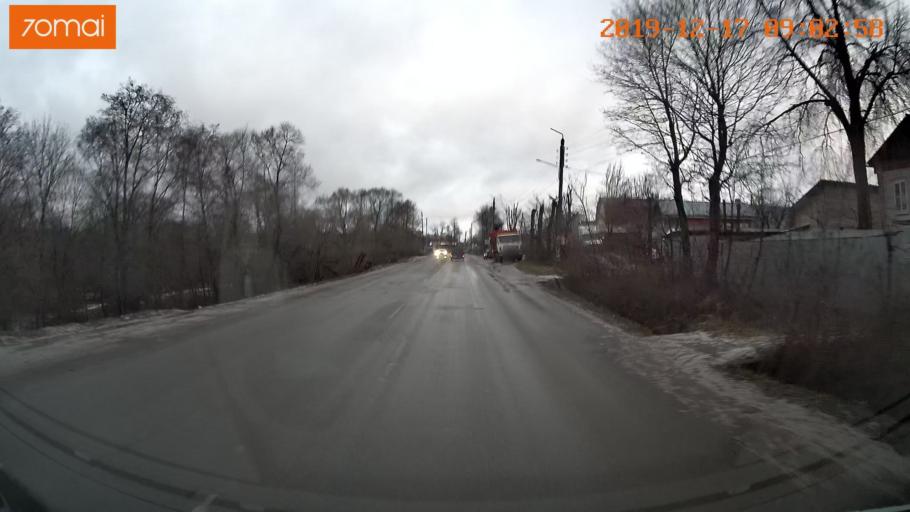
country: RU
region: Vladimir
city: Kosterevo
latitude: 55.9543
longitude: 39.6329
